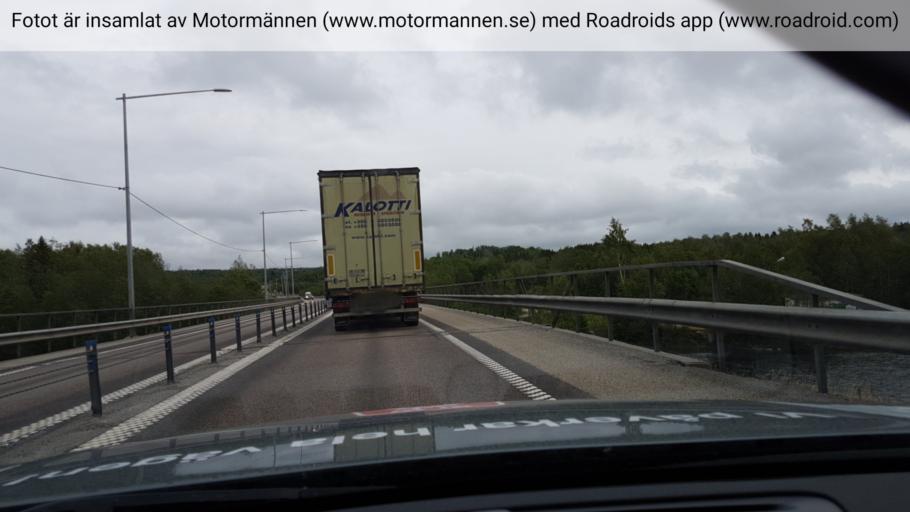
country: SE
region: Vaesternorrland
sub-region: Timra Kommun
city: Soraker
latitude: 62.5203
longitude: 17.4679
